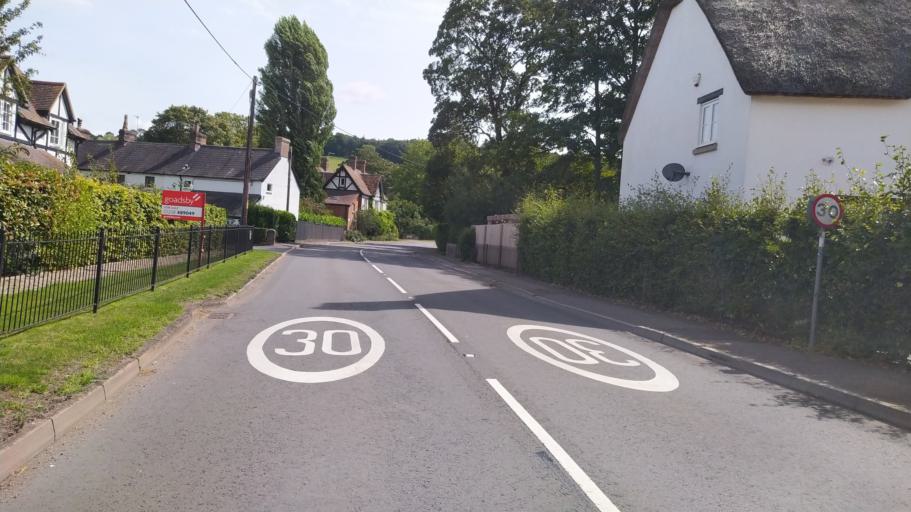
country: GB
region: England
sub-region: Dorset
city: Blandford Forum
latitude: 50.9271
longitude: -2.1927
